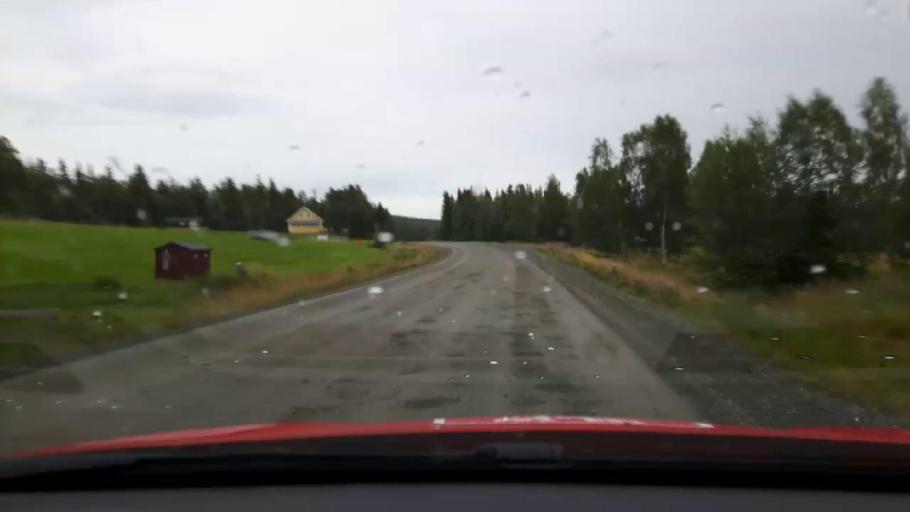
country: SE
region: Jaemtland
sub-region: Are Kommun
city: Are
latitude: 63.4644
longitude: 12.6215
